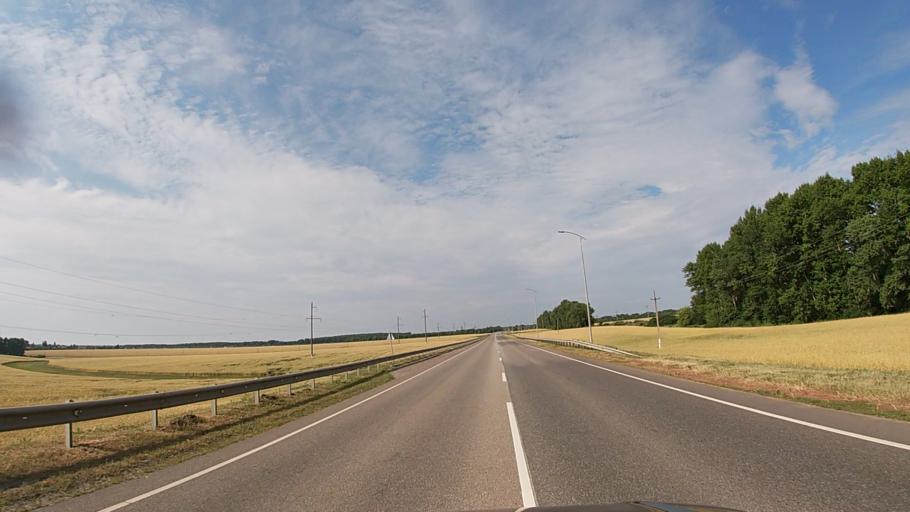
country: RU
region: Belgorod
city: Proletarskiy
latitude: 50.8120
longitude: 35.7483
